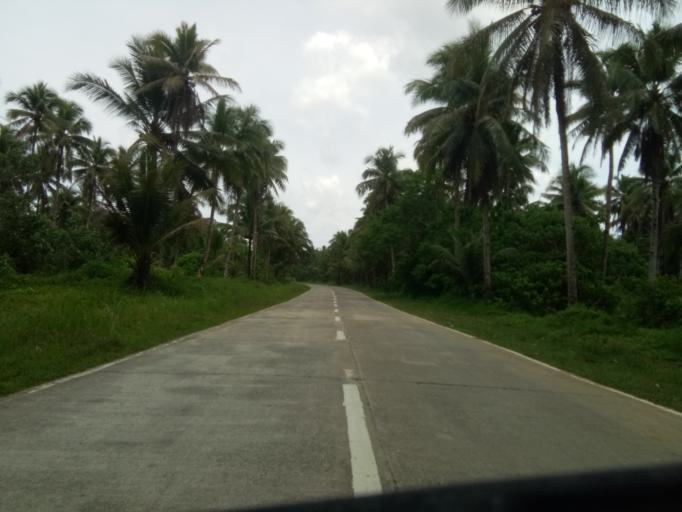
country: PH
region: Caraga
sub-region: Province of Surigao del Norte
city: San Isidro
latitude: 9.9257
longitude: 126.0530
